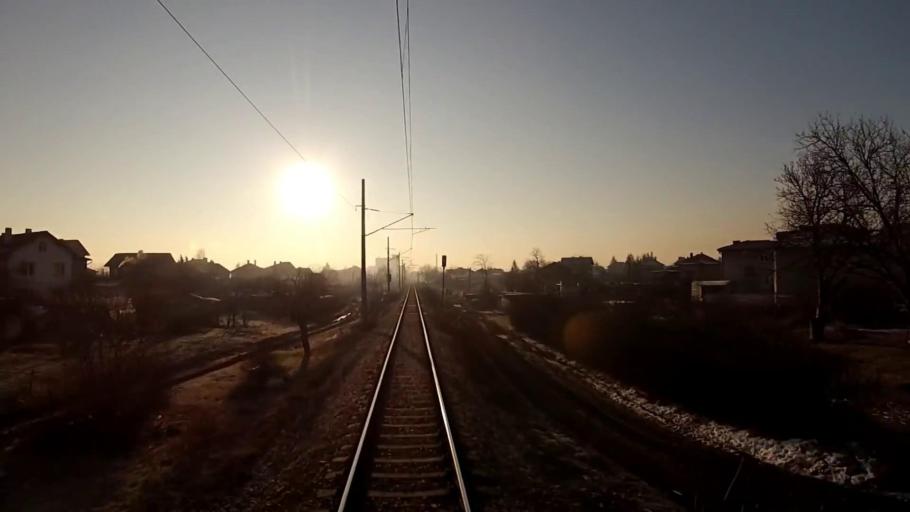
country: BG
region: Sofiya
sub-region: Obshtina Kostinbrod
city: Kostinbrod
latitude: 42.8042
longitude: 23.2018
